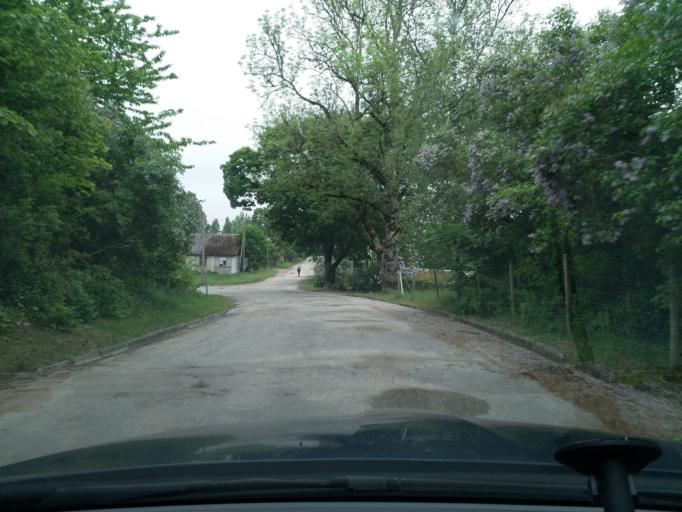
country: LV
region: Kuldigas Rajons
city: Kuldiga
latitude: 56.8813
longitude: 21.8221
